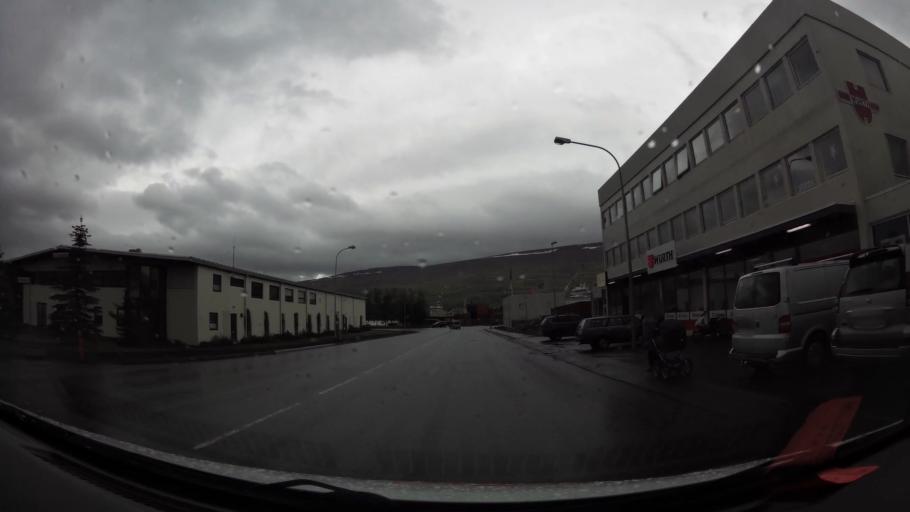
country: IS
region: Northeast
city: Akureyri
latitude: 65.6908
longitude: -18.0943
